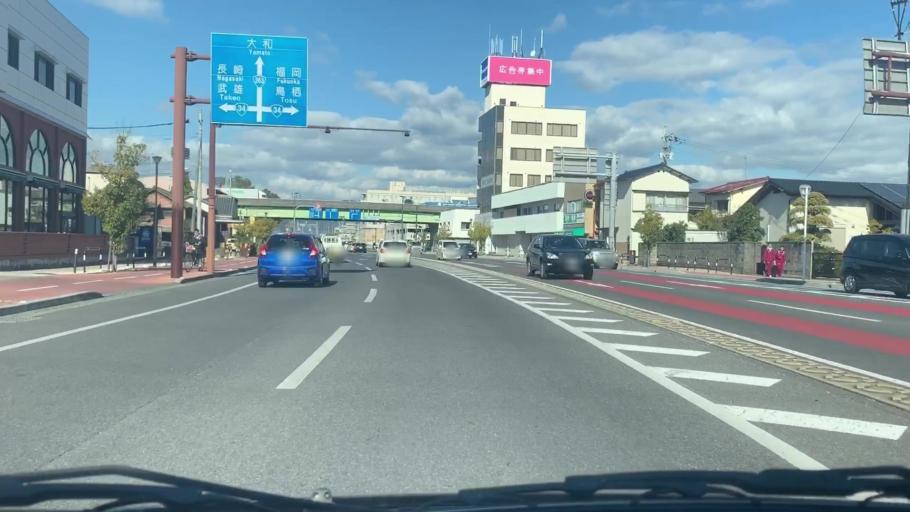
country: JP
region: Saga Prefecture
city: Saga-shi
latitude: 33.2729
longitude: 130.2941
